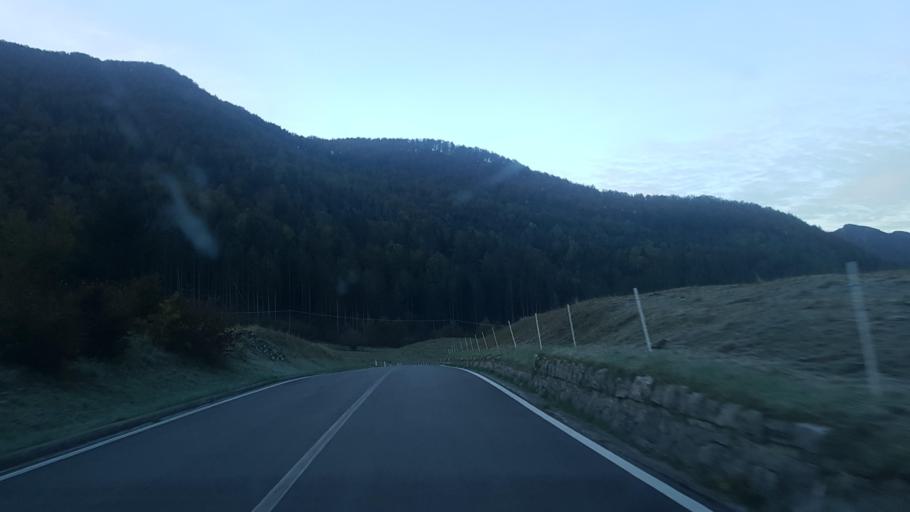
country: IT
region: Friuli Venezia Giulia
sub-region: Provincia di Udine
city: Villa Santina
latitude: 46.3549
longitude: 12.9316
